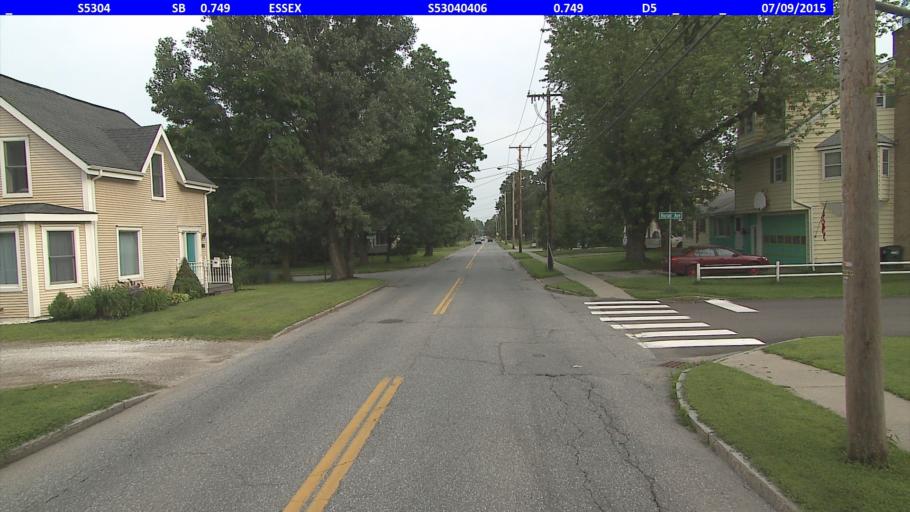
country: US
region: Vermont
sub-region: Chittenden County
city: Essex Junction
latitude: 44.4900
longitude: -73.1240
